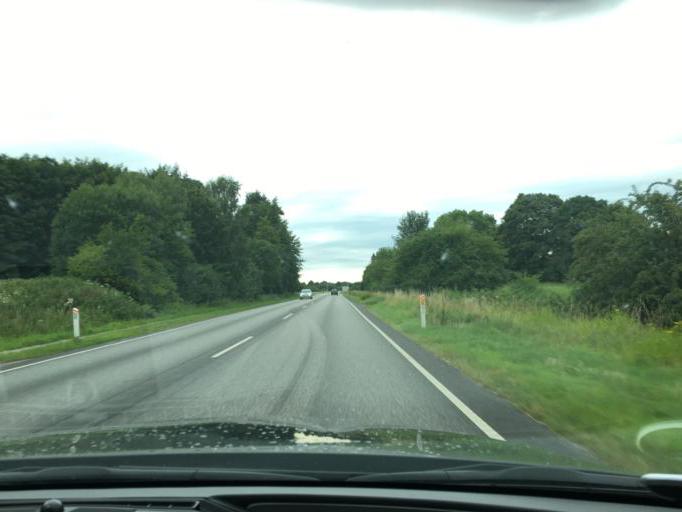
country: DK
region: Capital Region
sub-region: Horsholm Kommune
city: Horsholm
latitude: 55.8798
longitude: 12.4629
